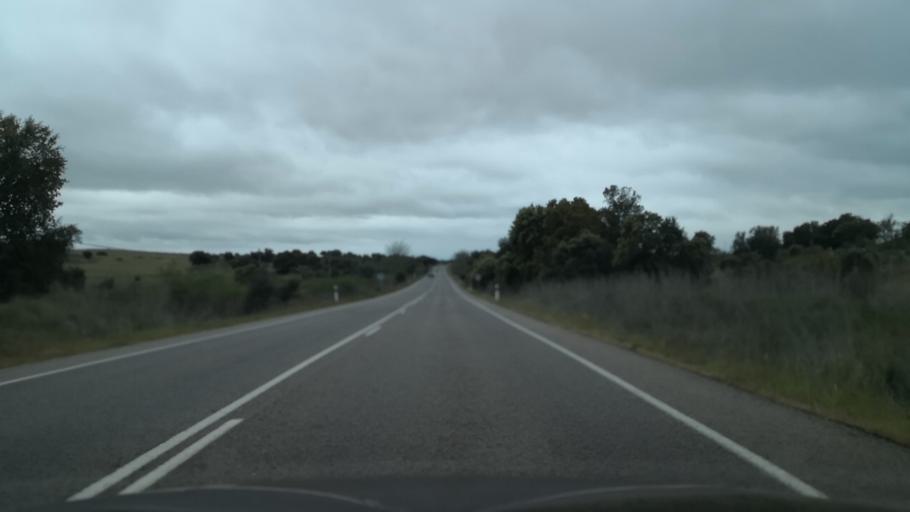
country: ES
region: Extremadura
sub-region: Provincia de Caceres
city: Caceres
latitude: 39.4170
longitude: -6.4137
